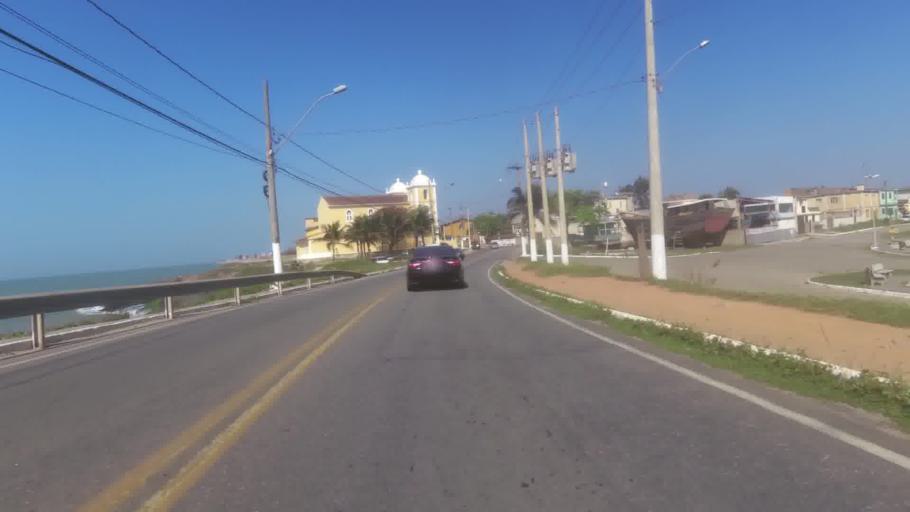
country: BR
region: Espirito Santo
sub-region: Itapemirim
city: Itapemirim
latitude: -21.0071
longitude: -40.8065
